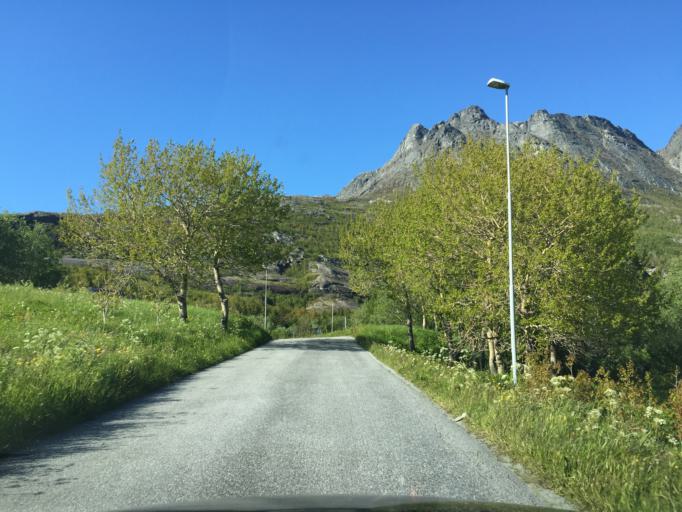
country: NO
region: Nordland
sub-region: Bodo
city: Loding
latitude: 67.4042
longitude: 14.6430
